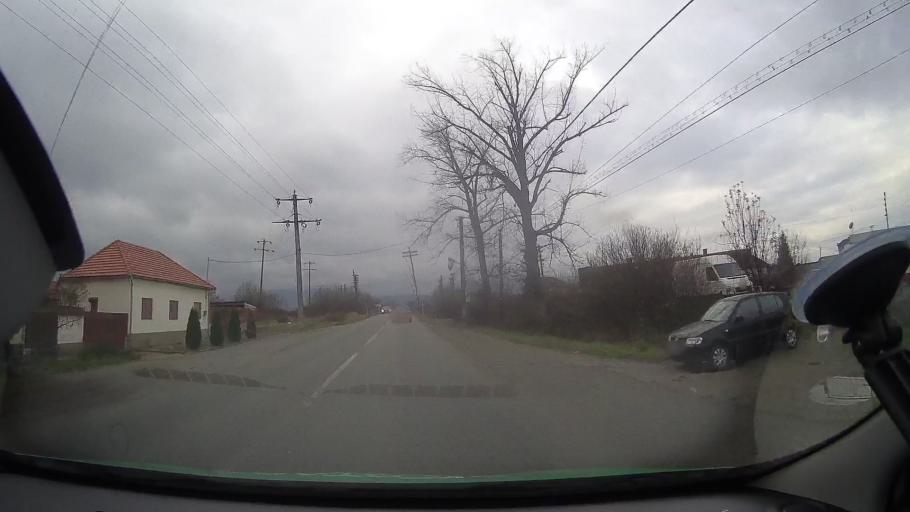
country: RO
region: Arad
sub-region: Comuna Sebis
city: Sebis
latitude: 46.3622
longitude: 22.1307
